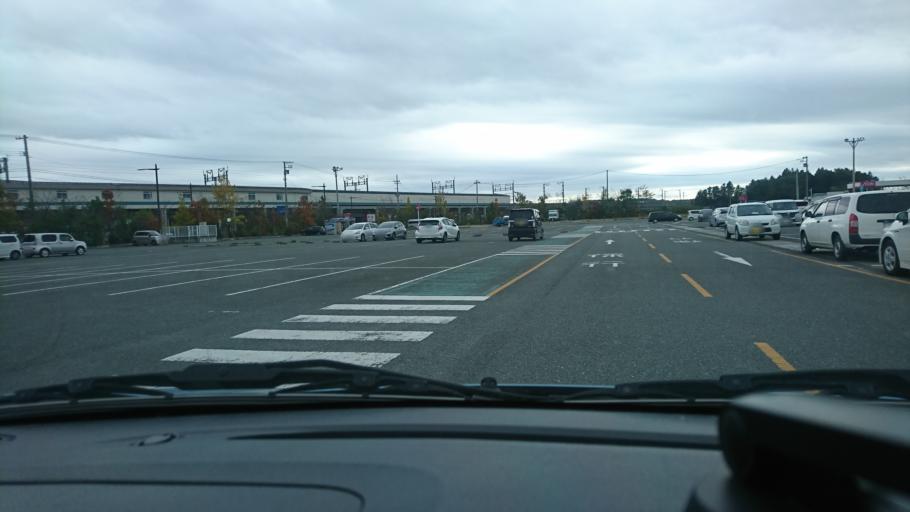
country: JP
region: Iwate
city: Ichinoseki
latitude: 38.7493
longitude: 141.0701
